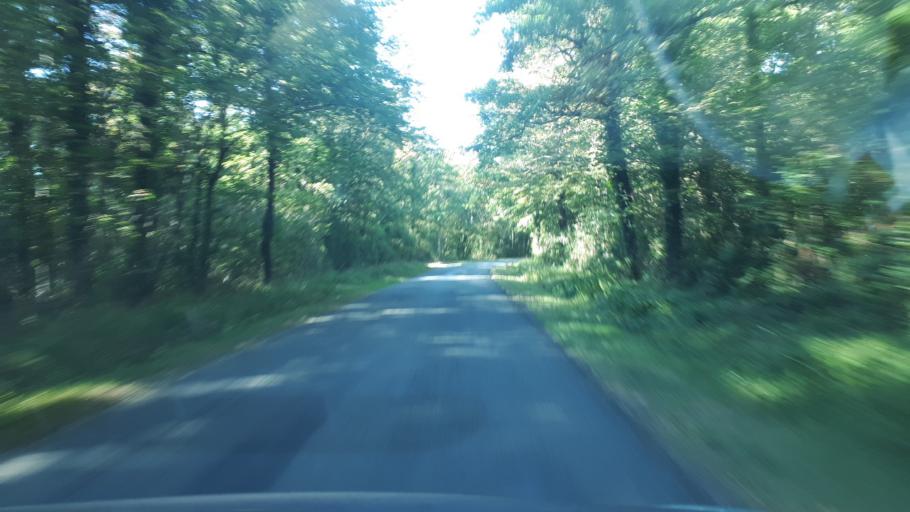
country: FR
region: Centre
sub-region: Departement du Cher
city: Sancerre
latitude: 47.2717
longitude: 2.7528
